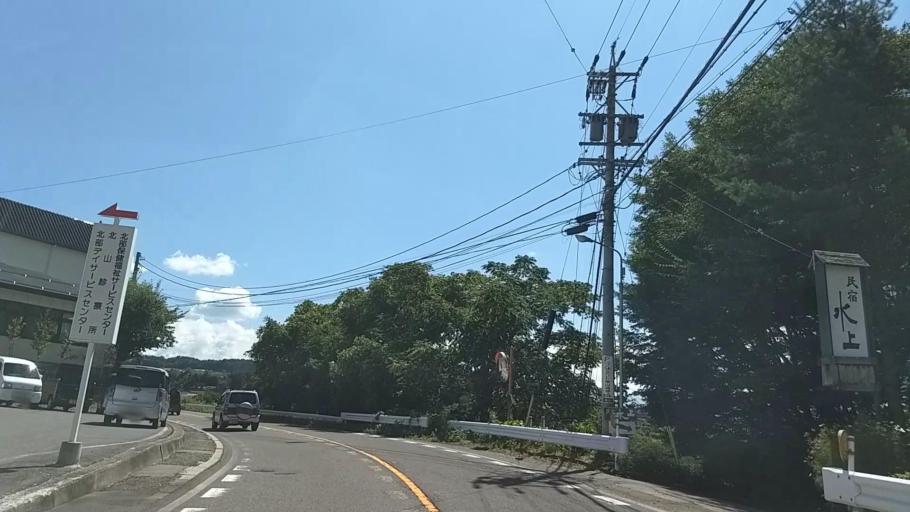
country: JP
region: Nagano
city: Chino
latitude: 36.0344
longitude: 138.2241
